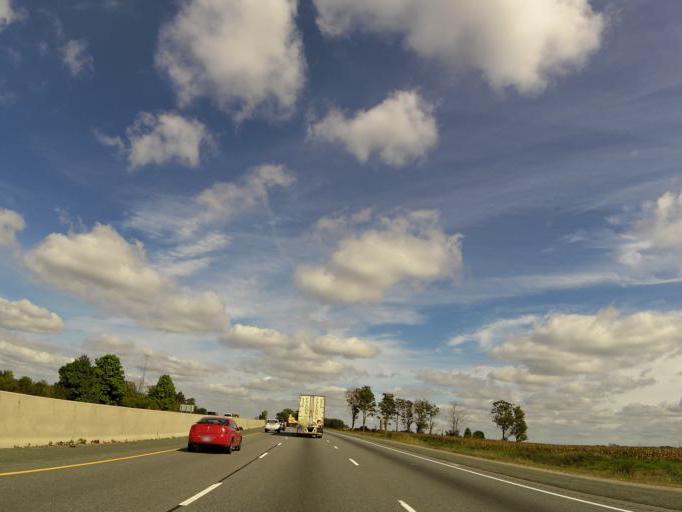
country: CA
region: Ontario
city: Ingersoll
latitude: 42.9812
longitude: -80.9205
